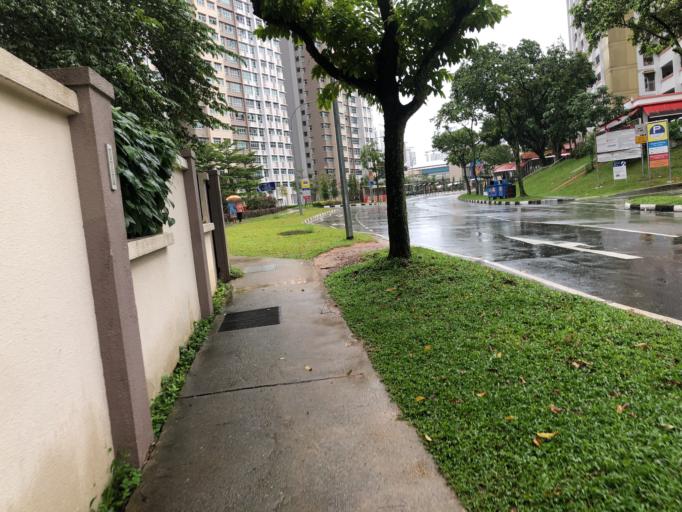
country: SG
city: Singapore
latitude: 1.3467
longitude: 103.7555
